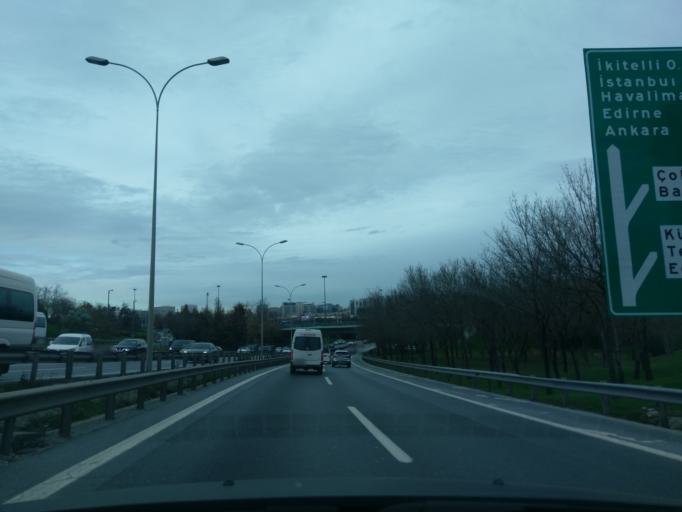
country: TR
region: Istanbul
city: Bahcelievler
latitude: 40.9913
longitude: 28.8183
